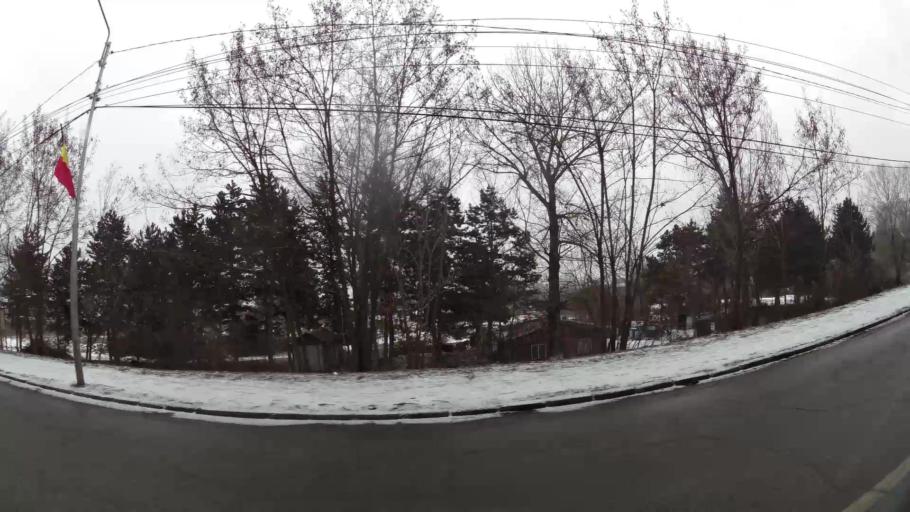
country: RO
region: Dambovita
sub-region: Municipiul Targoviste
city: Targoviste
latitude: 44.9390
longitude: 25.4571
